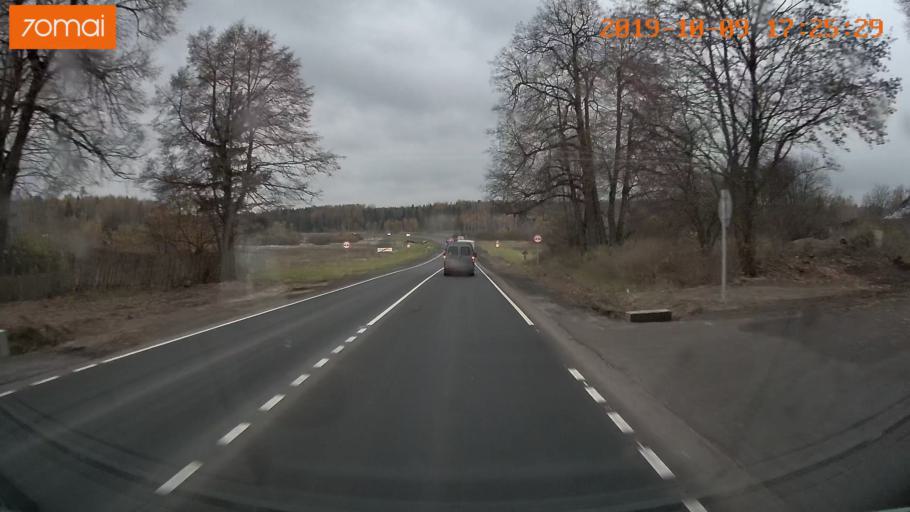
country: RU
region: Ivanovo
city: Furmanov
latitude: 57.1804
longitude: 41.0896
